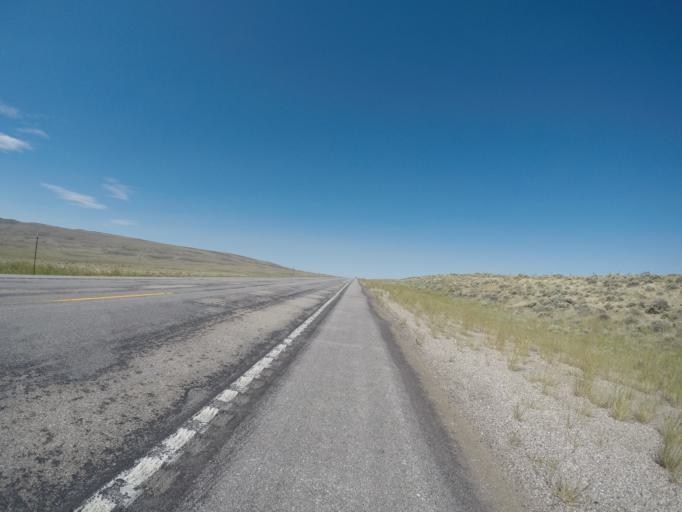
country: US
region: Wyoming
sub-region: Carbon County
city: Saratoga
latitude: 41.8001
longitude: -106.7115
